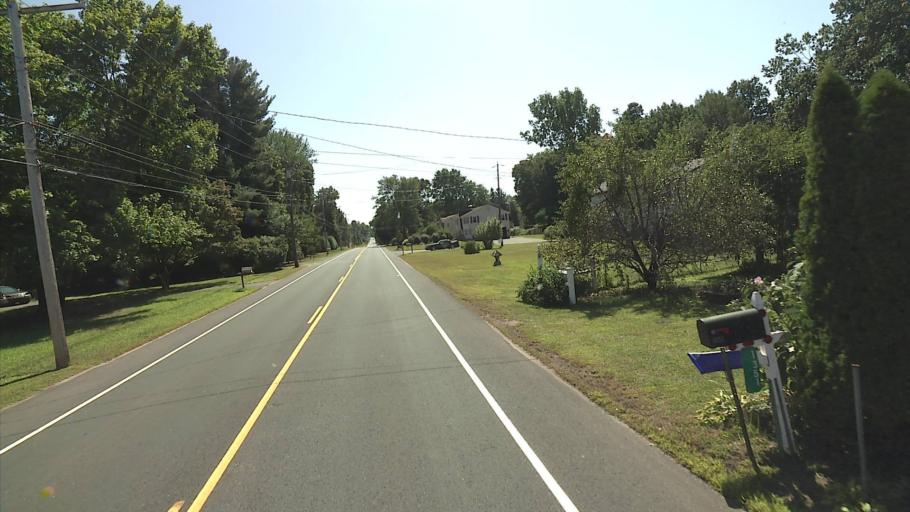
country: US
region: Connecticut
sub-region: Hartford County
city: Windsor Locks
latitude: 41.8986
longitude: -72.6260
